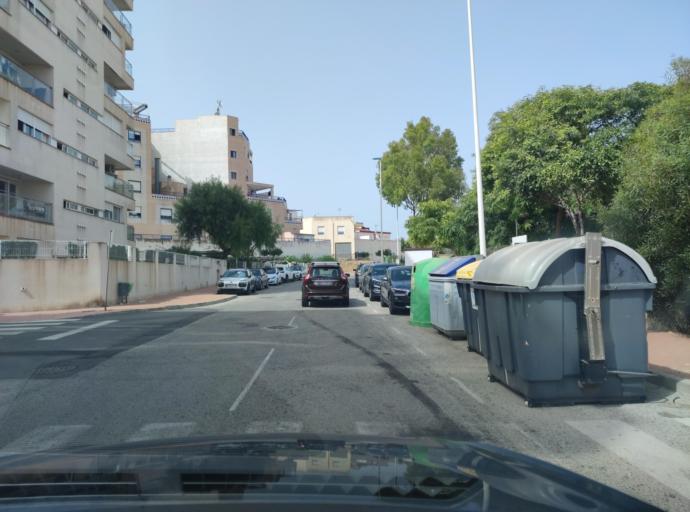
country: ES
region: Valencia
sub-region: Provincia de Alicante
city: Guardamar del Segura
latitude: 38.0961
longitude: -0.6570
